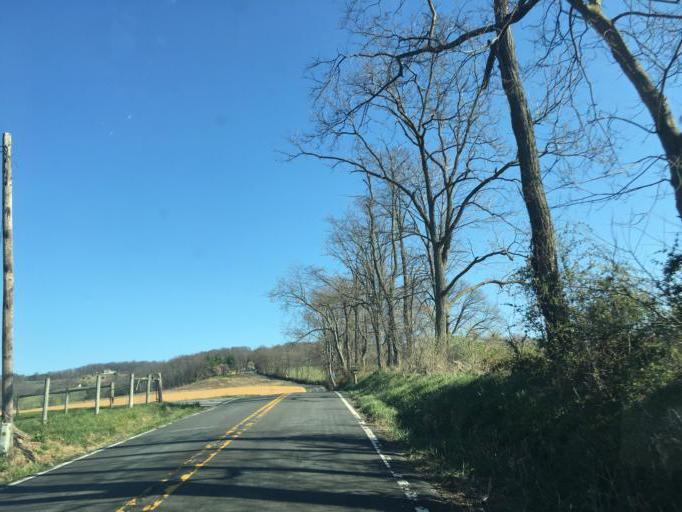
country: US
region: Maryland
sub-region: Frederick County
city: Myersville
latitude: 39.5392
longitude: -77.5453
